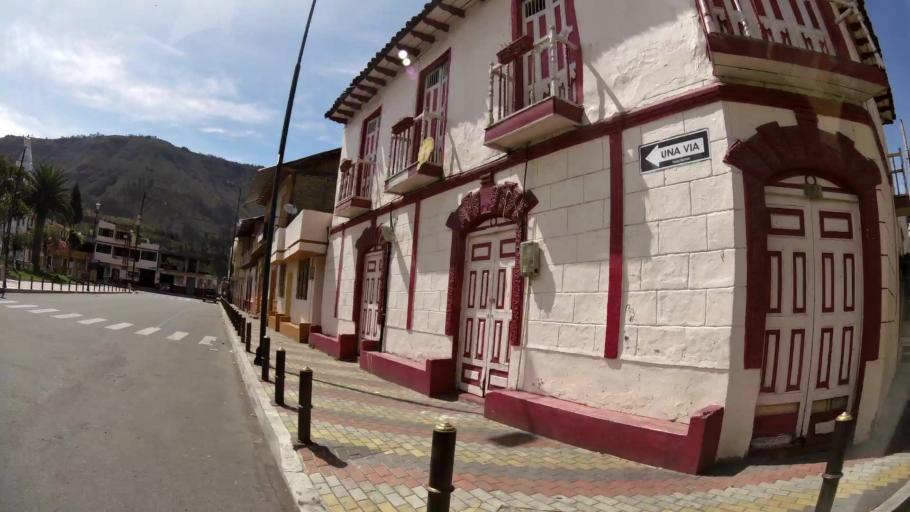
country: EC
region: Chimborazo
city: Guano
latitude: -1.5656
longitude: -78.5312
